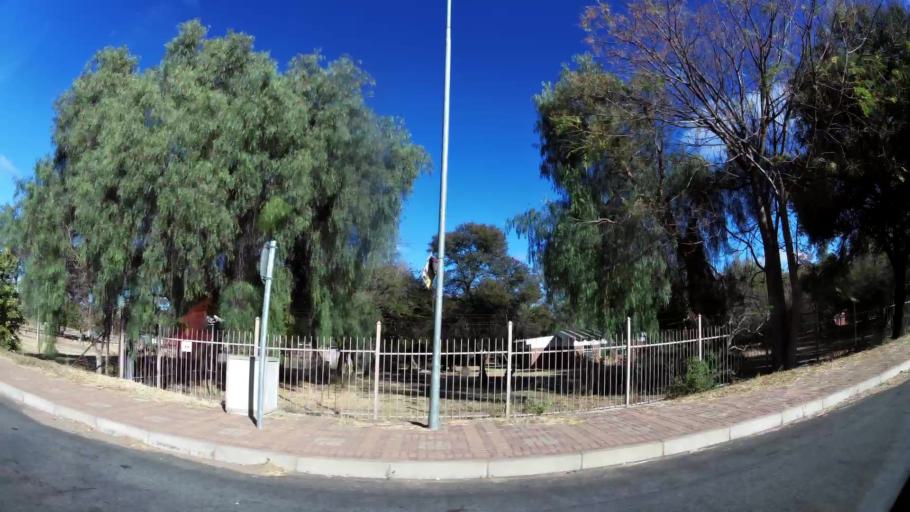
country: ZA
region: Limpopo
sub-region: Capricorn District Municipality
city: Polokwane
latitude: -23.9203
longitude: 29.4625
